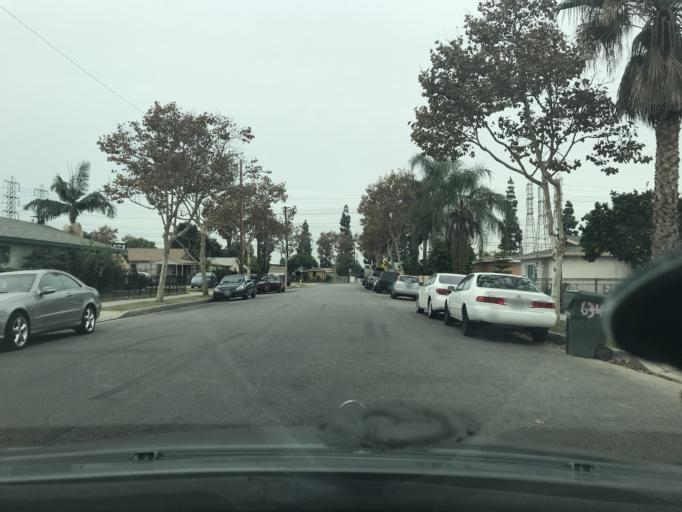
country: US
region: California
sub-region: Los Angeles County
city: Bell Gardens
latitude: 33.9609
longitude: -118.1532
